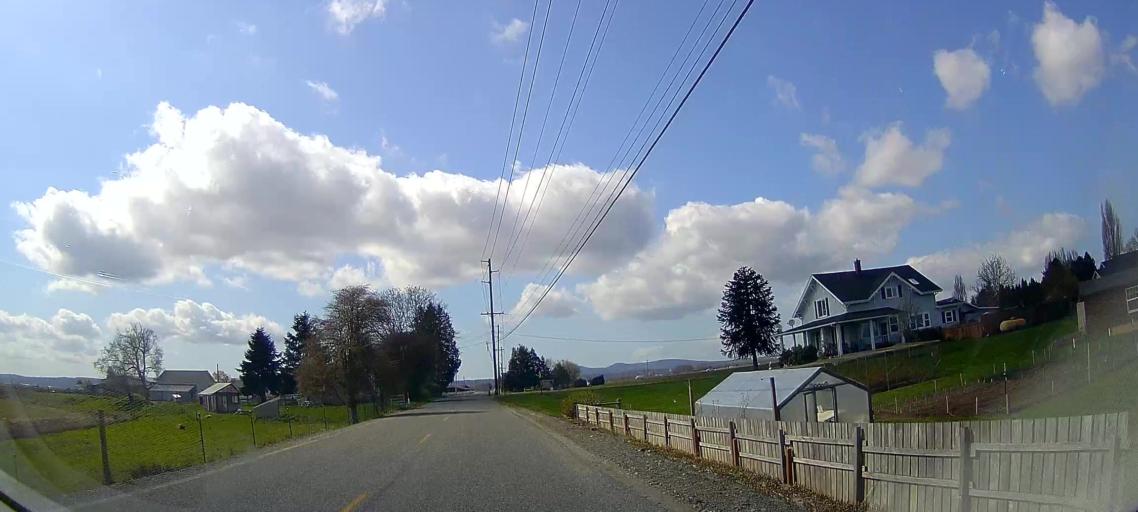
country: US
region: Washington
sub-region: Skagit County
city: Mount Vernon
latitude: 48.4426
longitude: -122.4385
